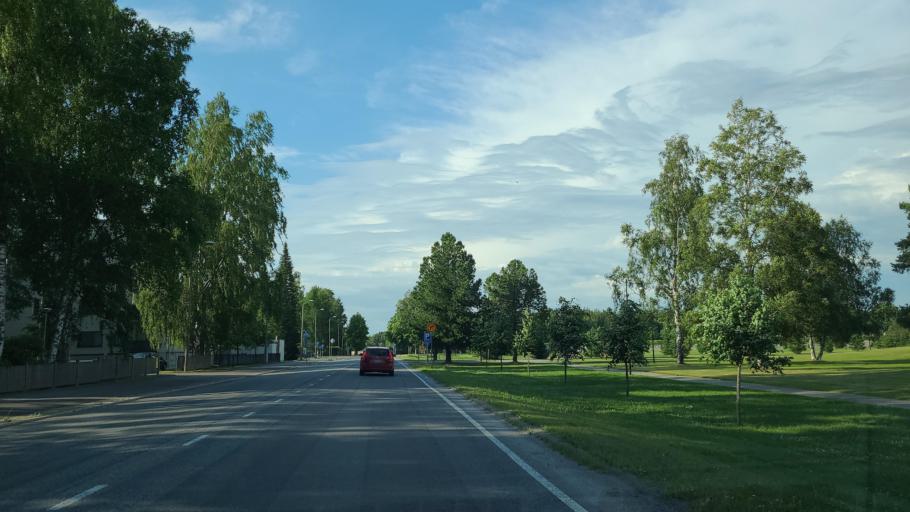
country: FI
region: Ostrobothnia
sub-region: Vaasa
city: Vaasa
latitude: 63.1058
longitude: 21.6178
